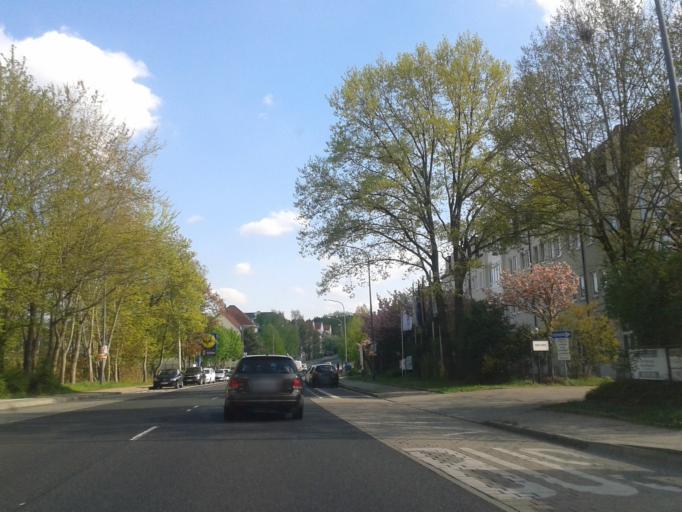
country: DE
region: Saxony
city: Albertstadt
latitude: 51.1138
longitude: 13.7732
